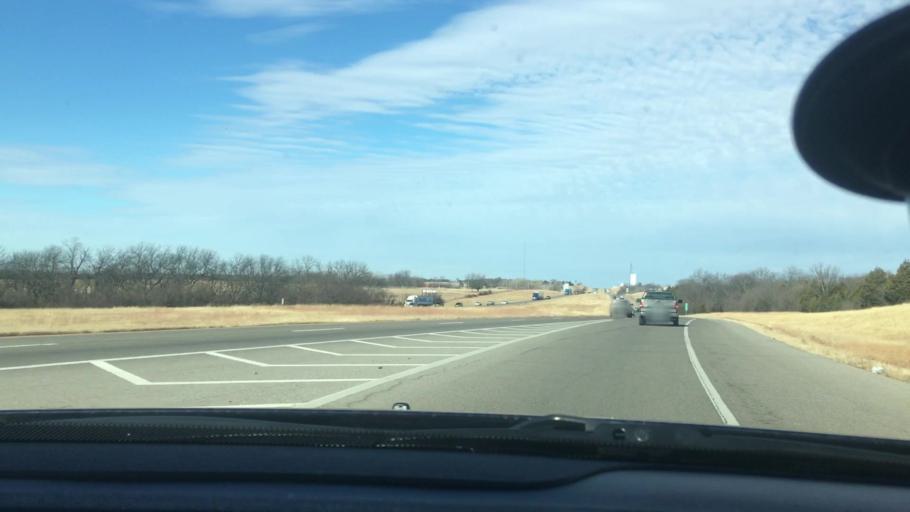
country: US
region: Oklahoma
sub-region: McClain County
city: Purcell
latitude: 35.0481
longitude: -97.3781
